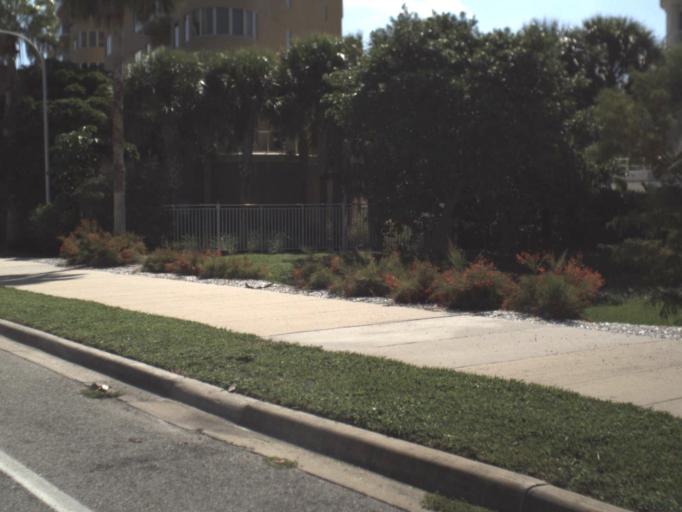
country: US
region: Florida
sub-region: Sarasota County
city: Sarasota
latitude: 27.3356
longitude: -82.5515
